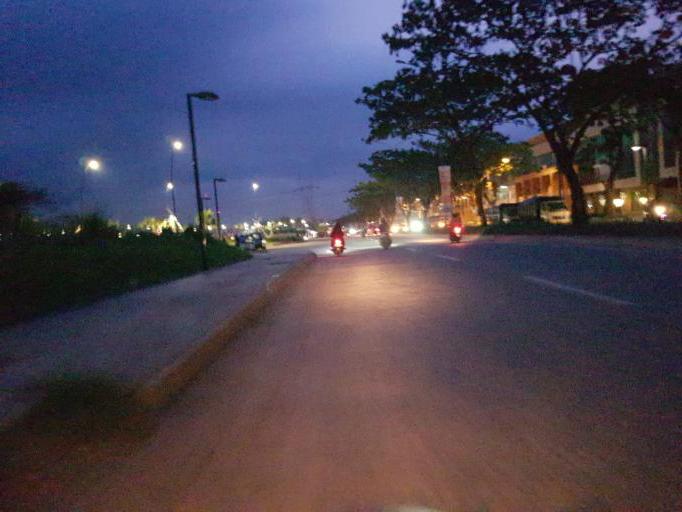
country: ID
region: West Java
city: Serpong
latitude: -6.3179
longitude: 106.6477
